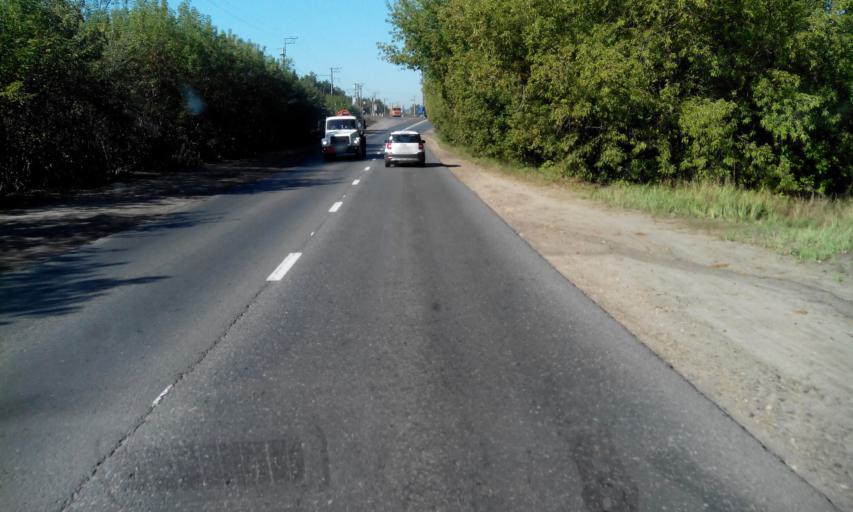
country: RU
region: Penza
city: Zarechnyy
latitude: 53.2091
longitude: 45.1167
